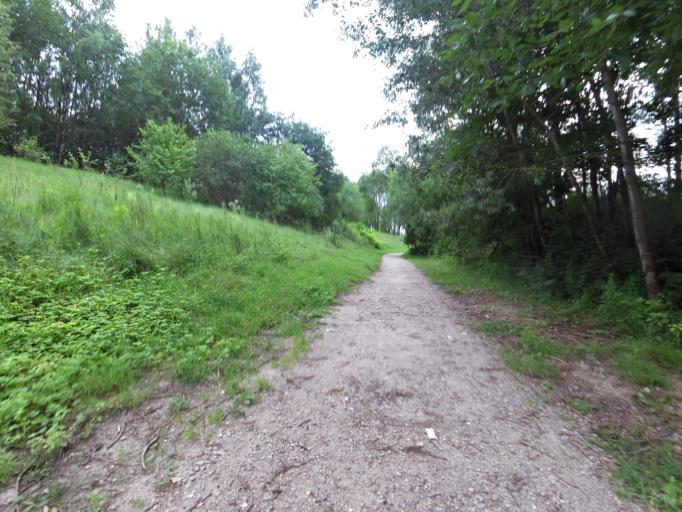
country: LT
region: Vilnius County
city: Seskine
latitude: 54.7156
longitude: 25.2649
